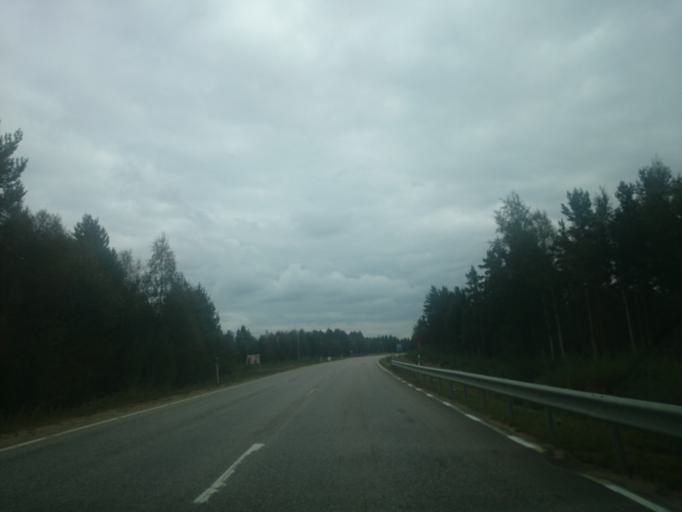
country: SE
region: Jaemtland
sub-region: Harjedalens Kommun
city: Sveg
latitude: 62.0458
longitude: 14.3453
